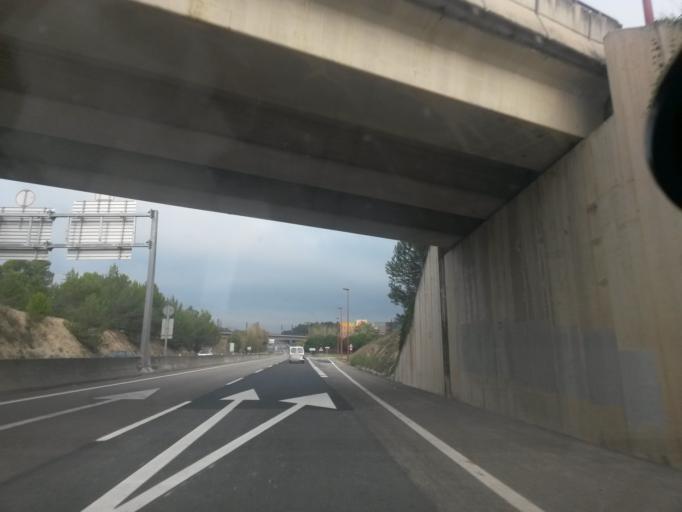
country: ES
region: Catalonia
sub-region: Provincia de Girona
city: Sarria de Ter
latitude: 42.0358
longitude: 2.8238
